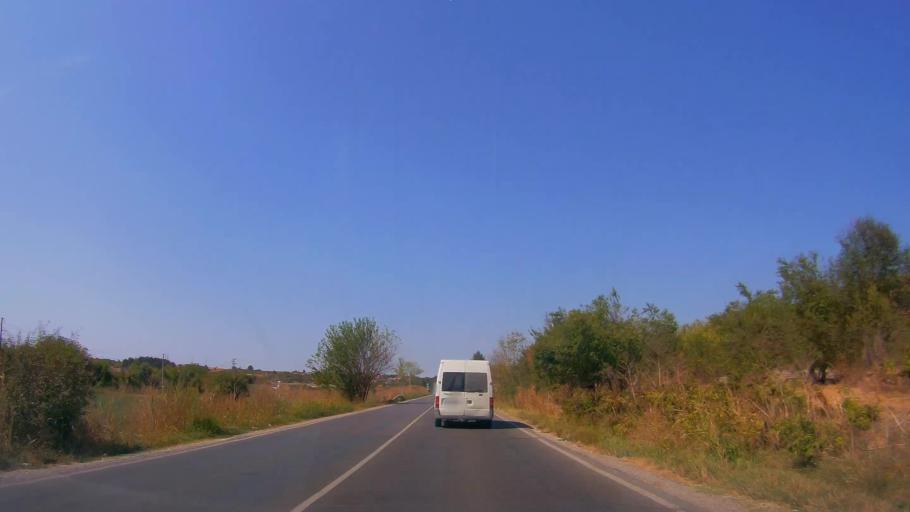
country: BG
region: Razgrad
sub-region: Obshtina Tsar Kaloyan
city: Tsar Kaloyan
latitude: 43.5989
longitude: 26.2480
